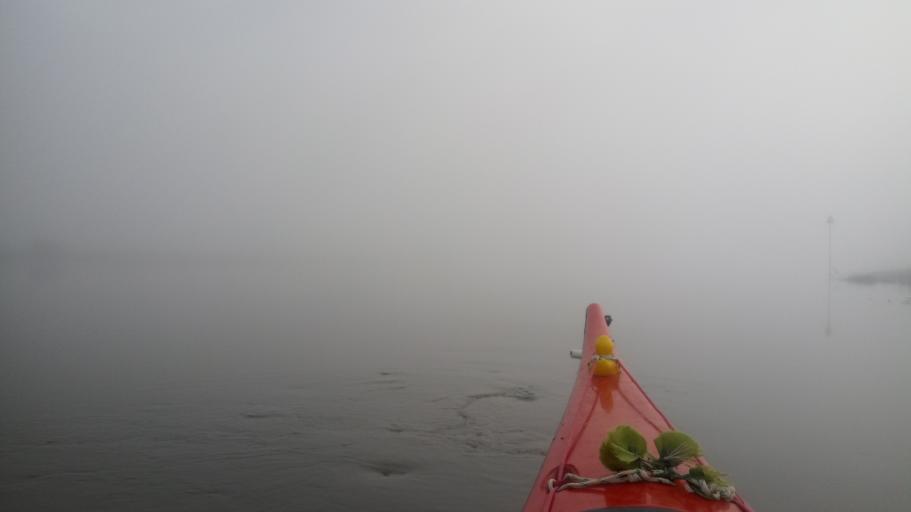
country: NL
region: Gelderland
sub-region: Gemeente Zutphen
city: Zutphen
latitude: 52.1127
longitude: 6.2088
